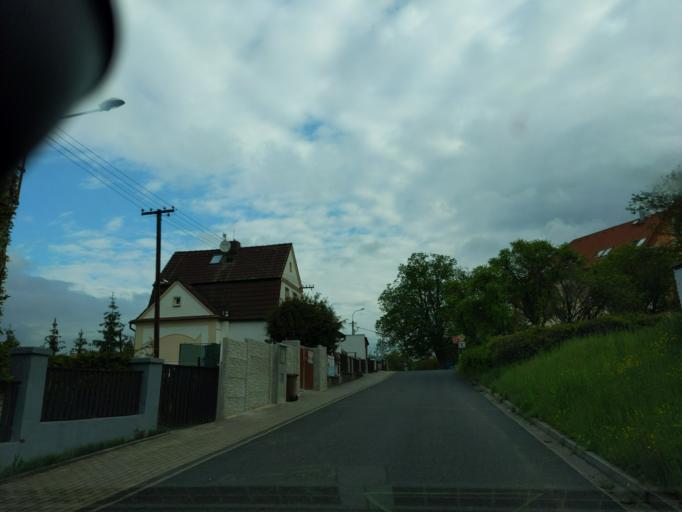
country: CZ
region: Ustecky
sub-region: Okres Usti nad Labem
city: Usti nad Labem
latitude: 50.6869
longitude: 14.0126
